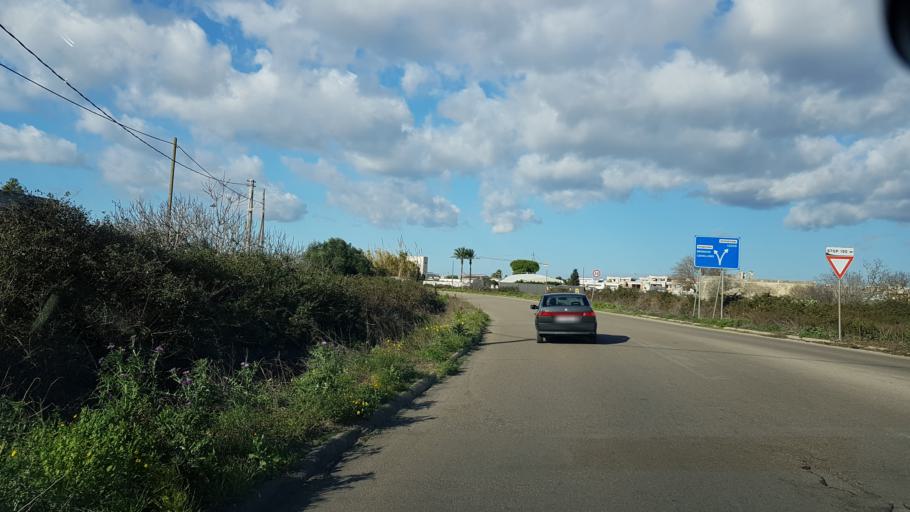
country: IT
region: Apulia
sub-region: Provincia di Lecce
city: Castromediano
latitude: 40.3280
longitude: 18.1854
